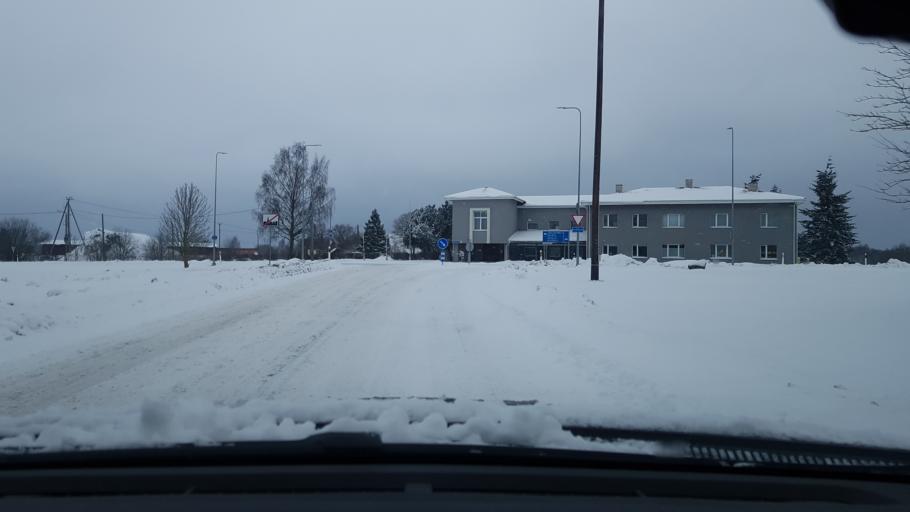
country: EE
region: Harju
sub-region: Kuusalu vald
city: Kuusalu
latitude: 59.4511
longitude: 25.3822
